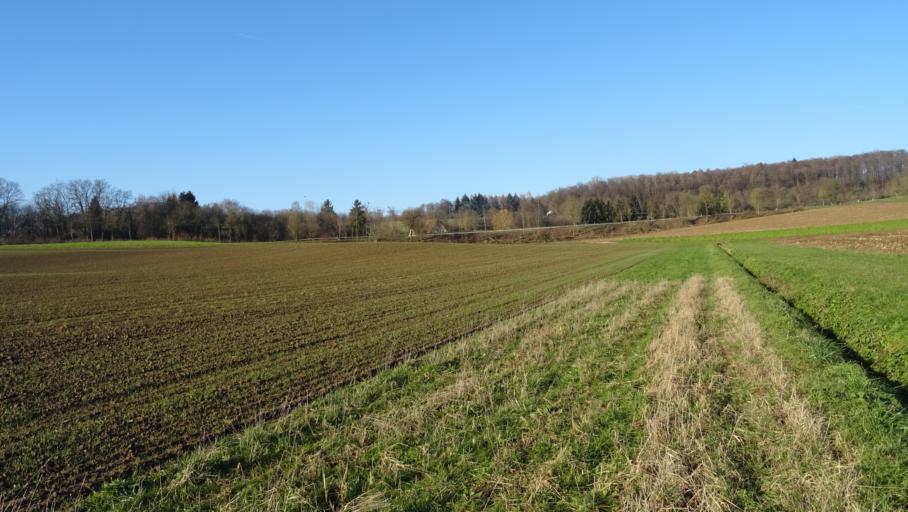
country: DE
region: Baden-Wuerttemberg
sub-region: Karlsruhe Region
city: Binau
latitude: 49.3455
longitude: 9.0364
